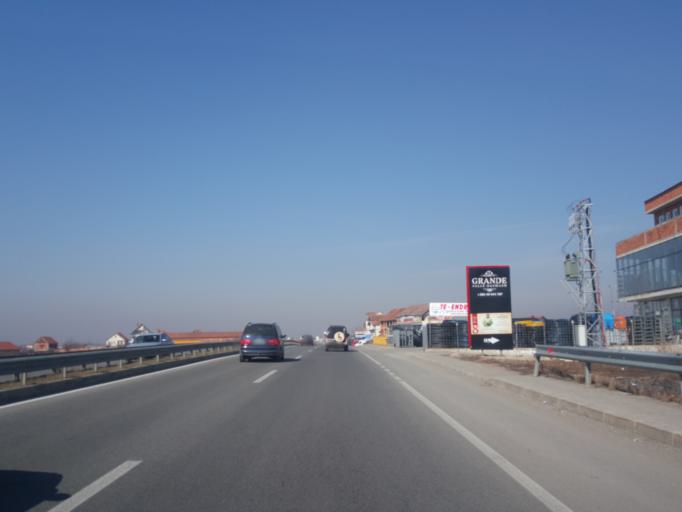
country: XK
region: Pristina
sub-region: Komuna e Obiliqit
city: Obiliq
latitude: 42.7518
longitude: 21.0403
